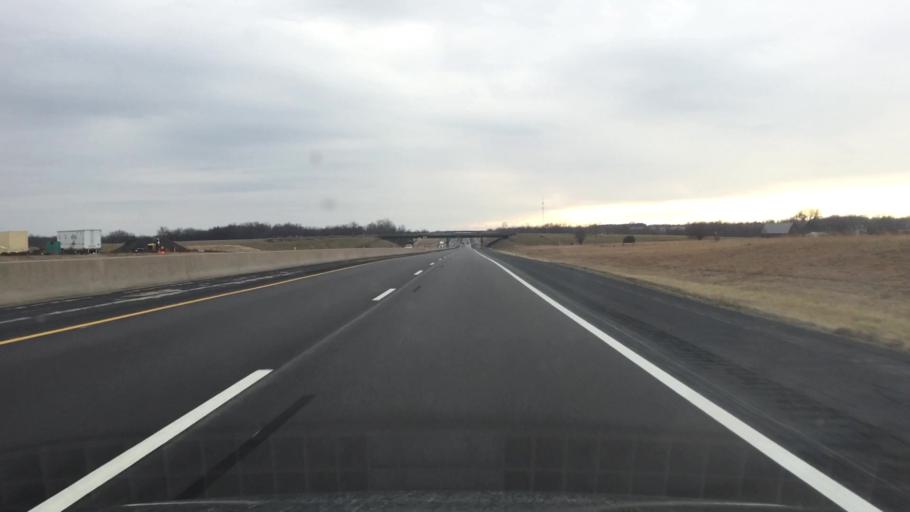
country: US
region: Kansas
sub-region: Osage County
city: Osage City
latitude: 38.7565
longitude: -95.9366
